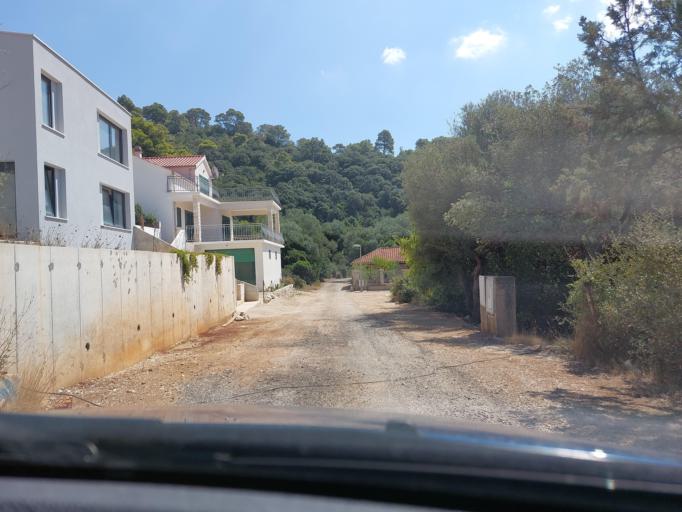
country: HR
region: Dubrovacko-Neretvanska
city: Smokvica
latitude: 42.7725
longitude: 16.8391
